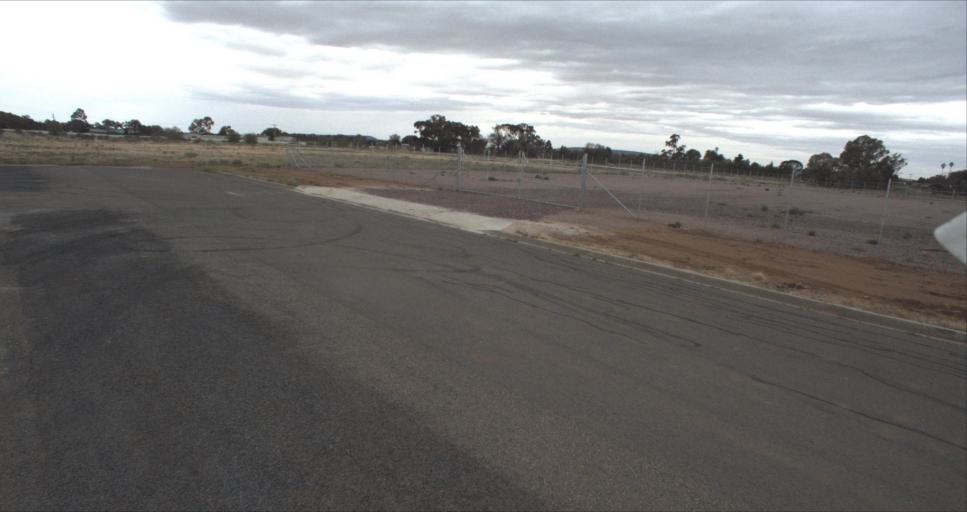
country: AU
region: New South Wales
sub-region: Leeton
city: Leeton
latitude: -34.5438
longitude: 146.3882
